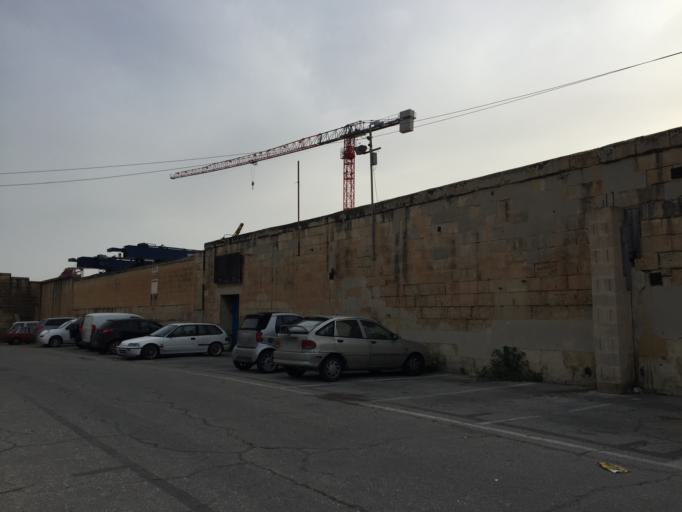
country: MT
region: L-Isla
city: Senglea
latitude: 35.8833
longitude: 14.5189
